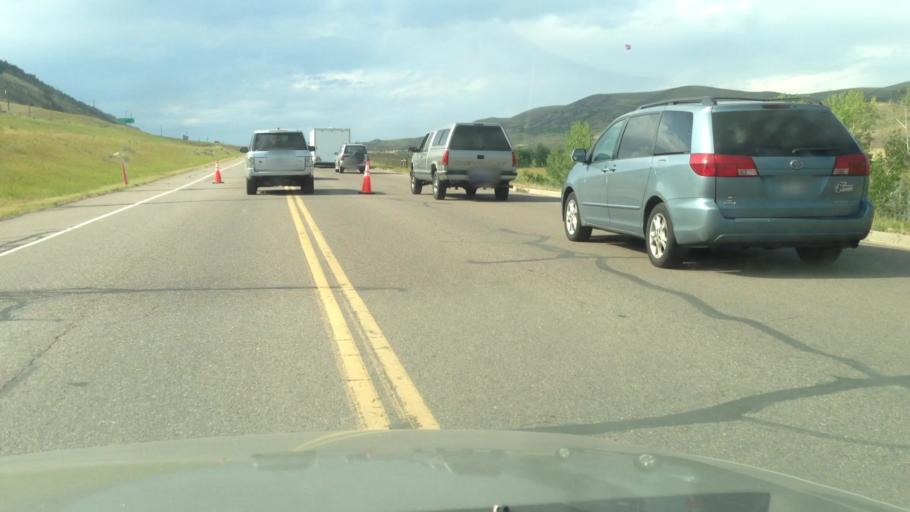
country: US
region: Colorado
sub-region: Jefferson County
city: West Pleasant View
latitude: 39.6695
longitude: -105.1867
